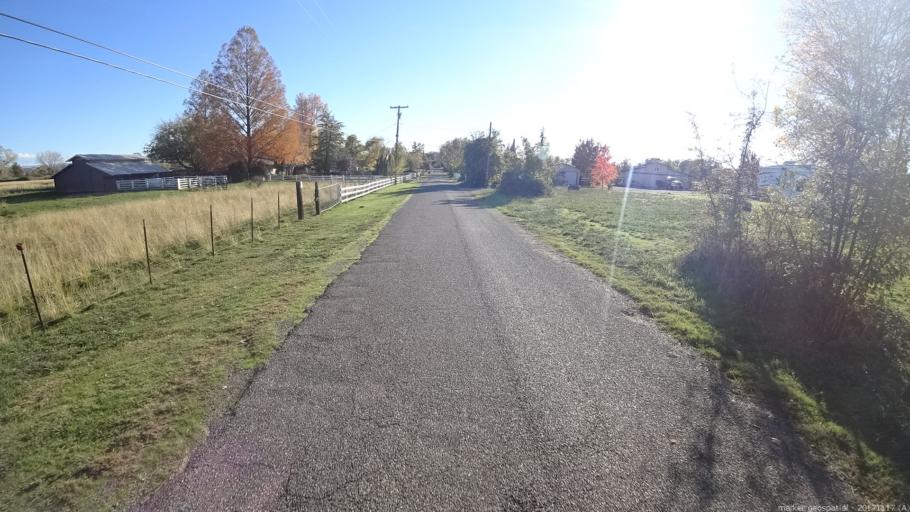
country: US
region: California
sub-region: Shasta County
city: Cottonwood
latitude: 40.3978
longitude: -122.2167
